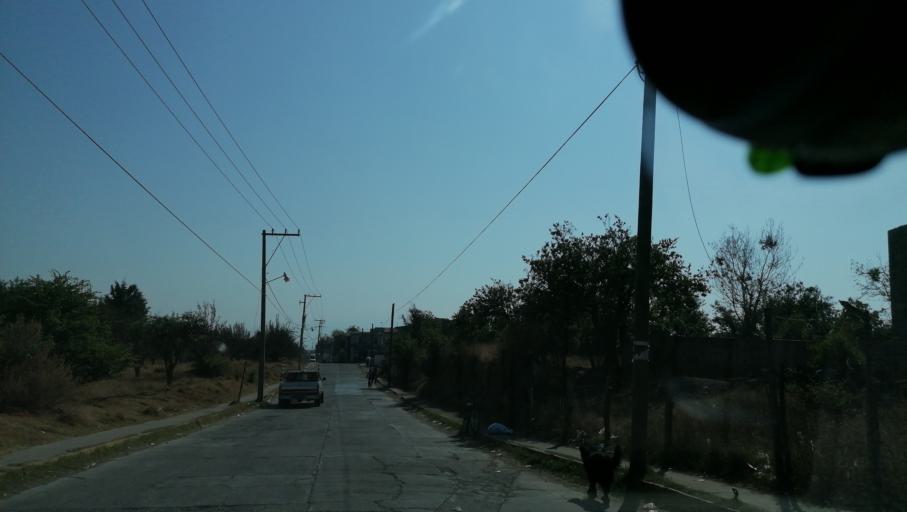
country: MX
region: Puebla
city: Domingo Arenas
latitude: 19.1427
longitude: -98.4532
